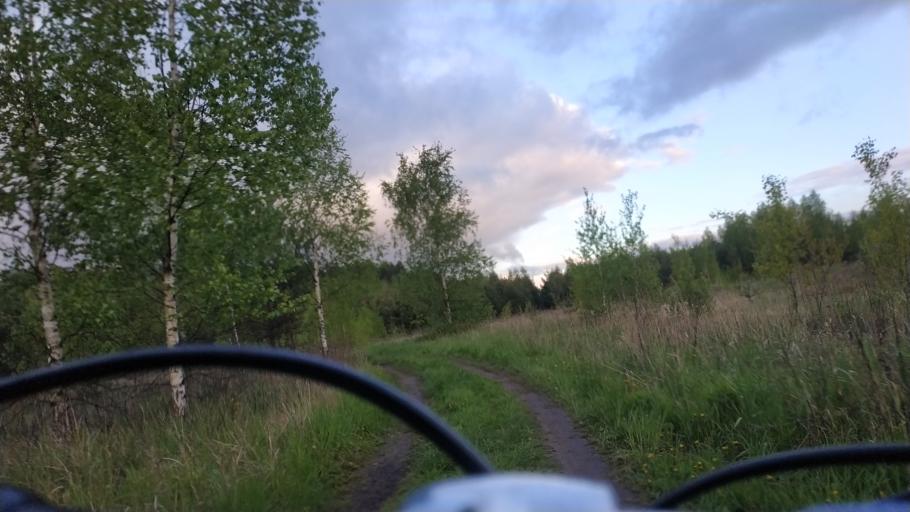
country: RU
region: Moskovskaya
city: Ramenskoye
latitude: 55.5973
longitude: 38.2849
